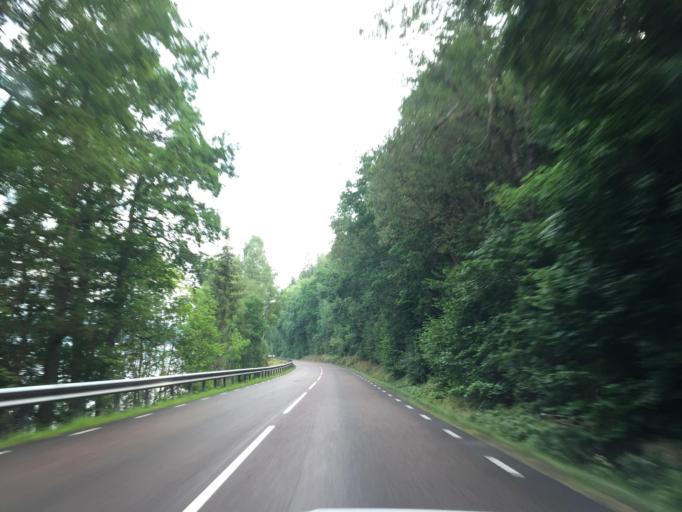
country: SE
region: Vaestra Goetaland
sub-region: Alingsas Kommun
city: Ingared
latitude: 57.8537
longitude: 12.5408
